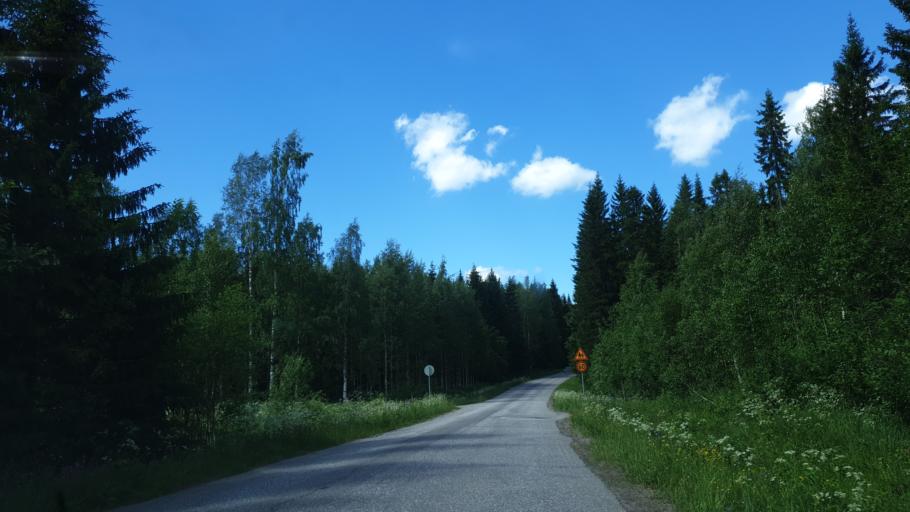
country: FI
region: Northern Savo
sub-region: Koillis-Savo
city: Kaavi
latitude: 63.0214
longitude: 28.6463
